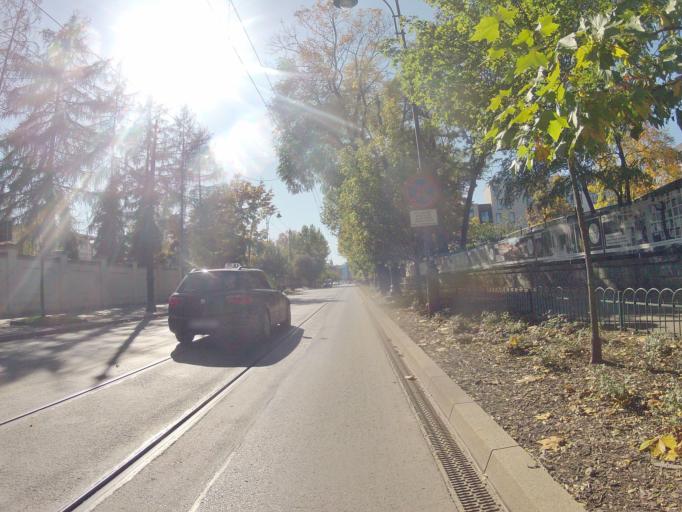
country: PL
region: Lesser Poland Voivodeship
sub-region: Krakow
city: Krakow
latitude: 50.0706
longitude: 19.9543
